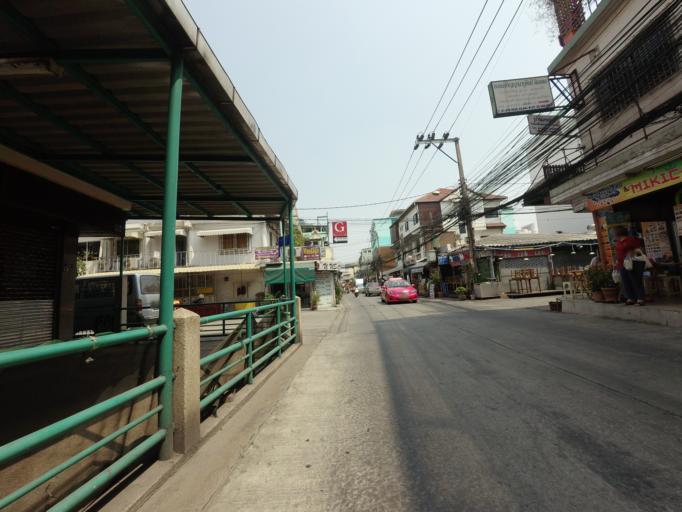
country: TH
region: Bangkok
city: Din Daeng
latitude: 13.7632
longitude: 100.5633
